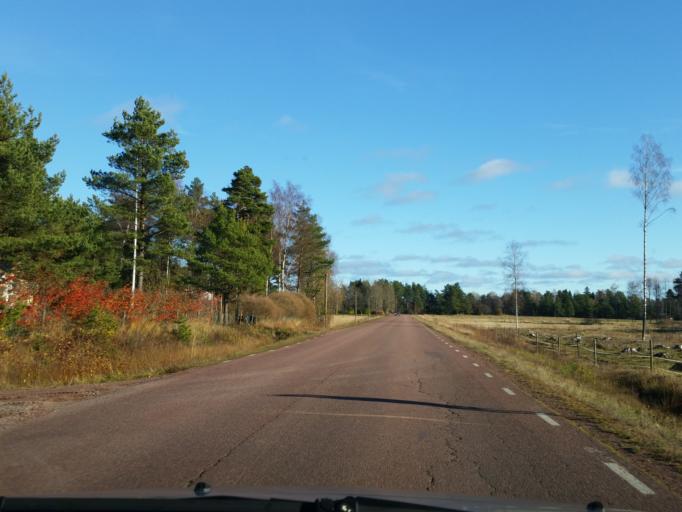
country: AX
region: Alands landsbygd
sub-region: Jomala
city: Jomala
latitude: 60.1581
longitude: 19.9146
